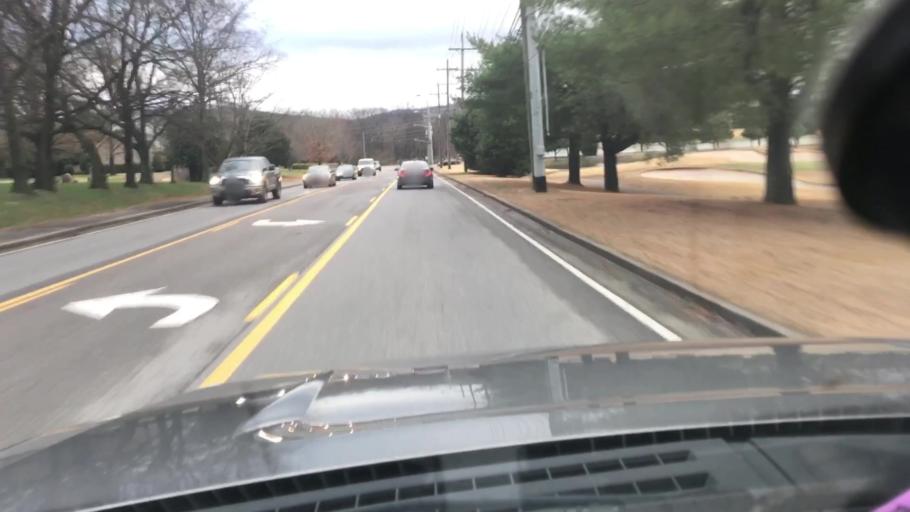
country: US
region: Tennessee
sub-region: Williamson County
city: Brentwood Estates
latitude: 35.9643
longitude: -86.7873
